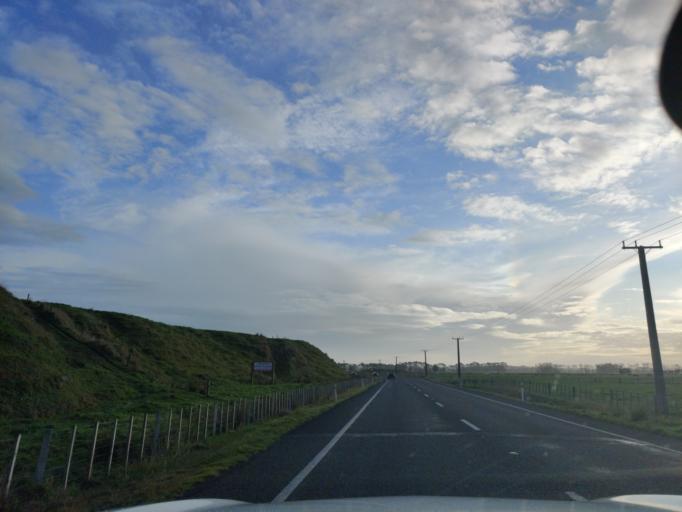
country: NZ
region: Manawatu-Wanganui
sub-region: Palmerston North City
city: Palmerston North
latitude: -40.4898
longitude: 175.4972
